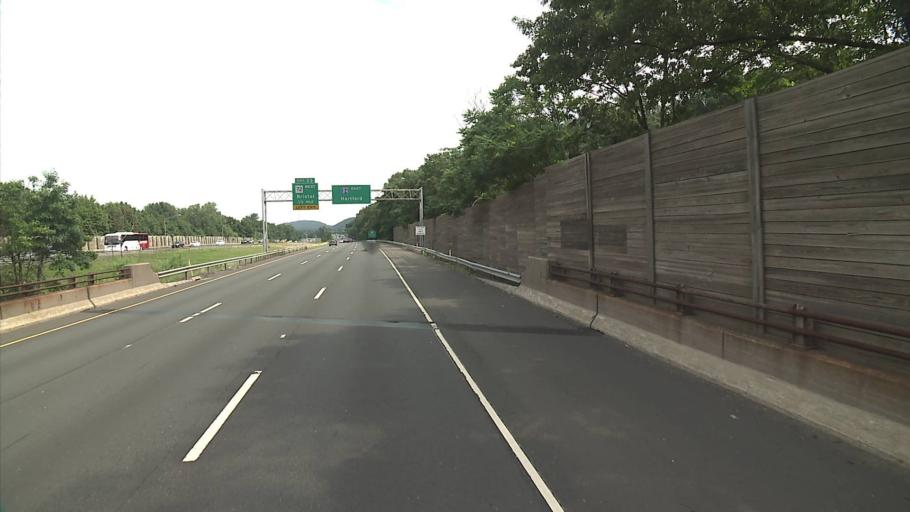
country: US
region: Connecticut
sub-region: Hartford County
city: Plainville
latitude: 41.6603
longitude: -72.8489
